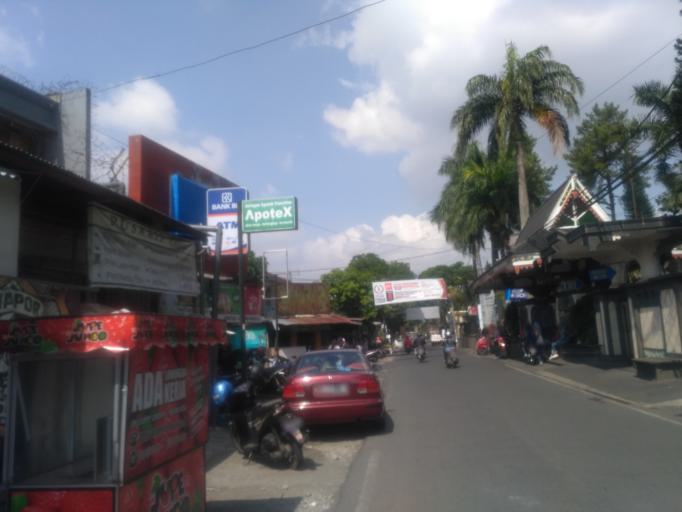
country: ID
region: East Java
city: Malang
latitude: -7.9418
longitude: 112.6382
